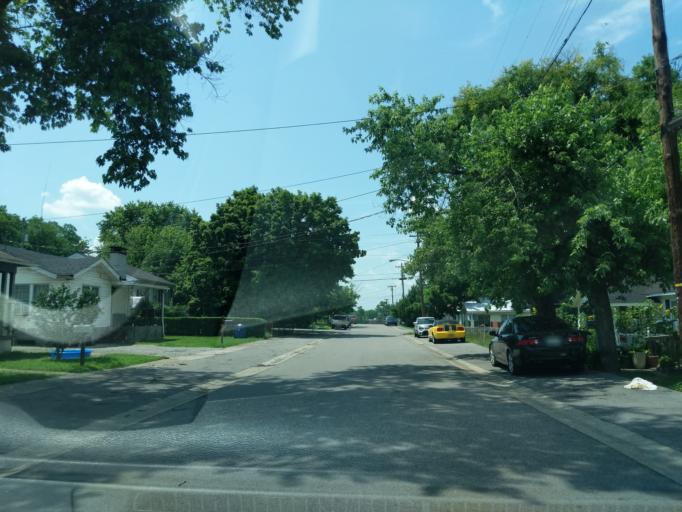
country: US
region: Tennessee
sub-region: Davidson County
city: Lakewood
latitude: 36.2473
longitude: -86.6389
